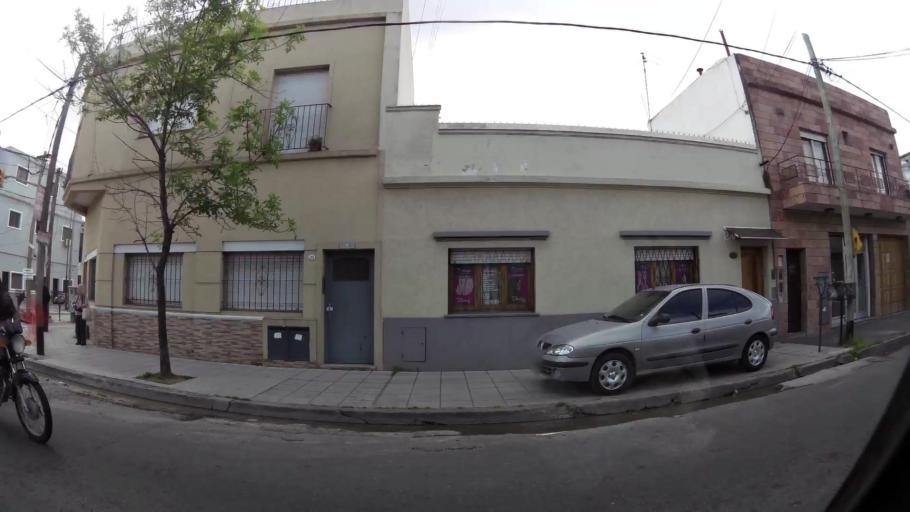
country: AR
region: Buenos Aires
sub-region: Partido de Lanus
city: Lanus
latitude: -34.6952
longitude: -58.3747
